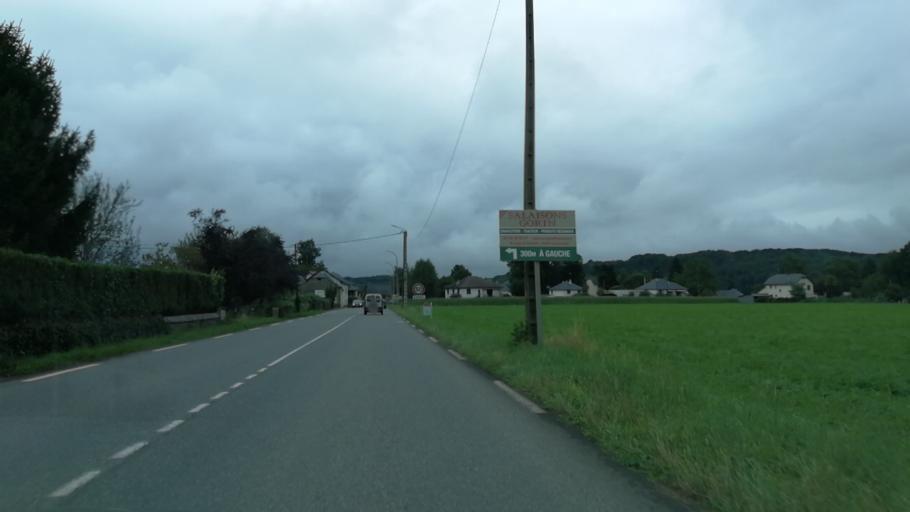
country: FR
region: Aquitaine
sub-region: Departement des Pyrenees-Atlantiques
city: Oloron-Sainte-Marie
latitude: 43.1521
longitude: -0.5979
